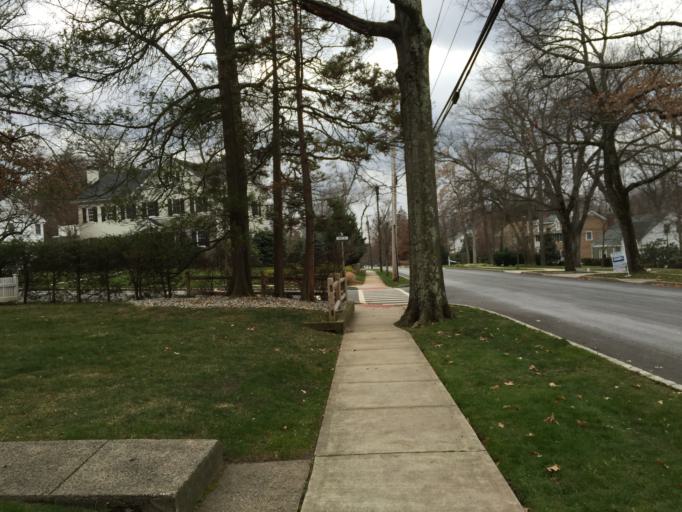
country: US
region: New Jersey
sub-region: Morris County
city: Chatham
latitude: 40.7165
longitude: -74.3752
